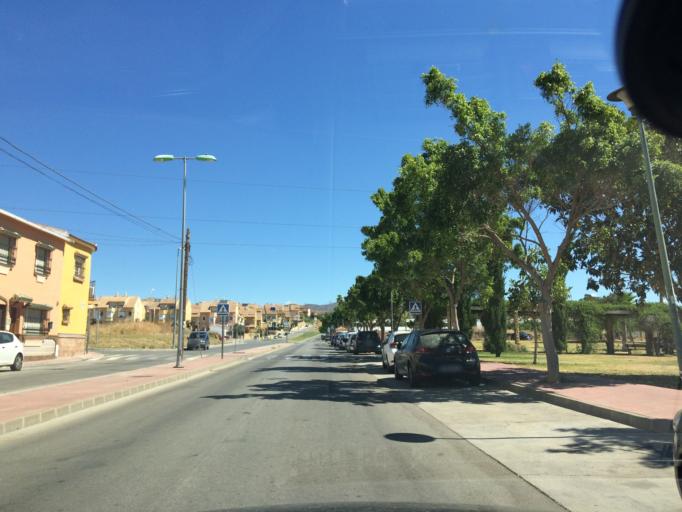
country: ES
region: Andalusia
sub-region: Provincia de Malaga
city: Estacion de Cartama
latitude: 36.7382
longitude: -4.6077
